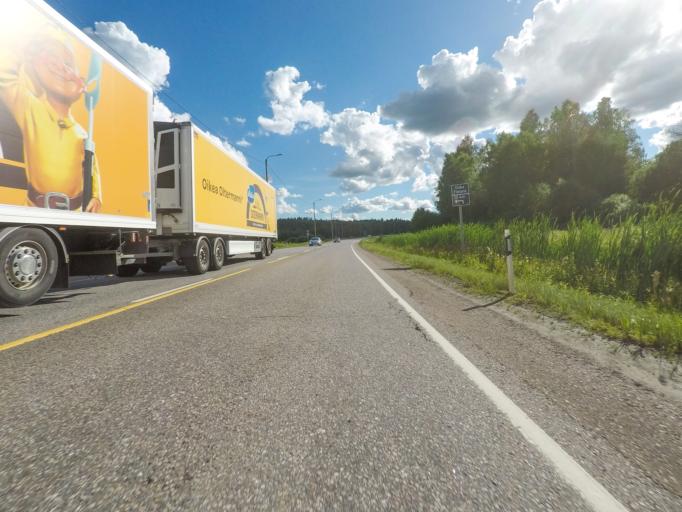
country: FI
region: Uusimaa
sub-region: Helsinki
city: Vihti
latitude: 60.4484
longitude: 24.5156
